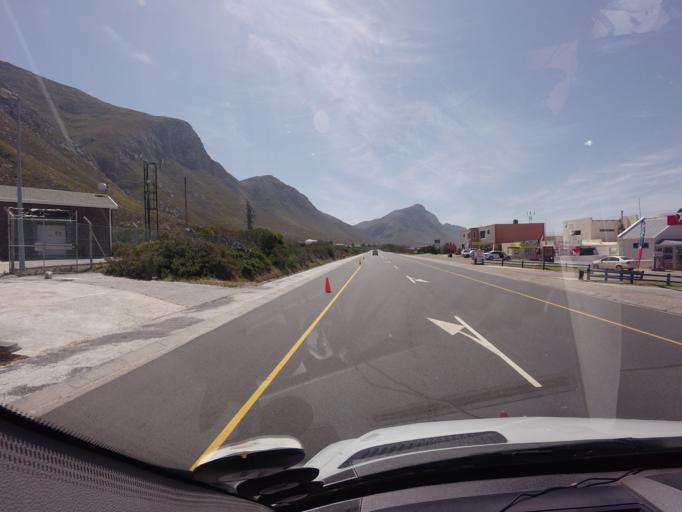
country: ZA
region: Western Cape
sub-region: Overberg District Municipality
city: Grabouw
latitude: -34.3563
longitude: 18.8985
